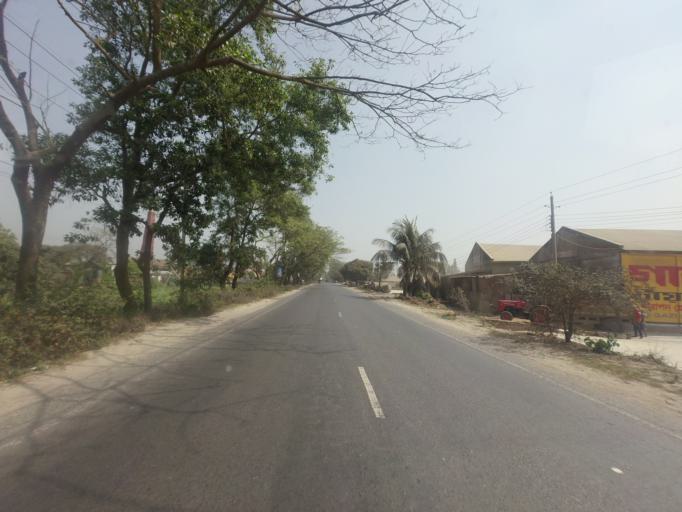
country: BD
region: Dhaka
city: Bhairab Bazar
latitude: 24.0409
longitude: 91.0403
